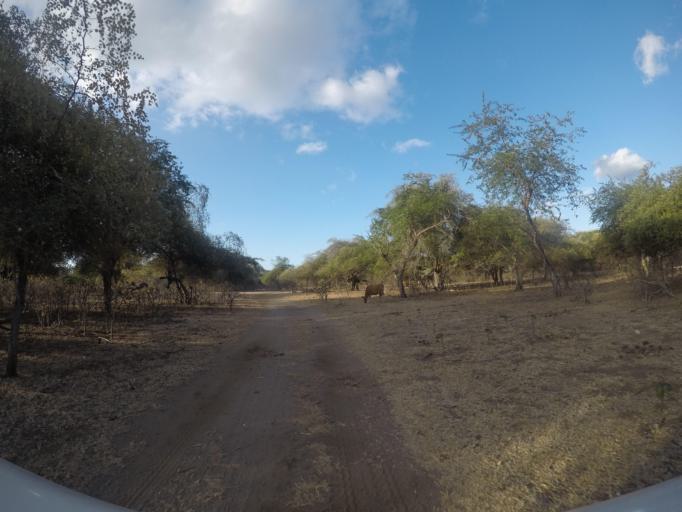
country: TL
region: Lautem
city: Lospalos
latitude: -8.3284
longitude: 126.9779
